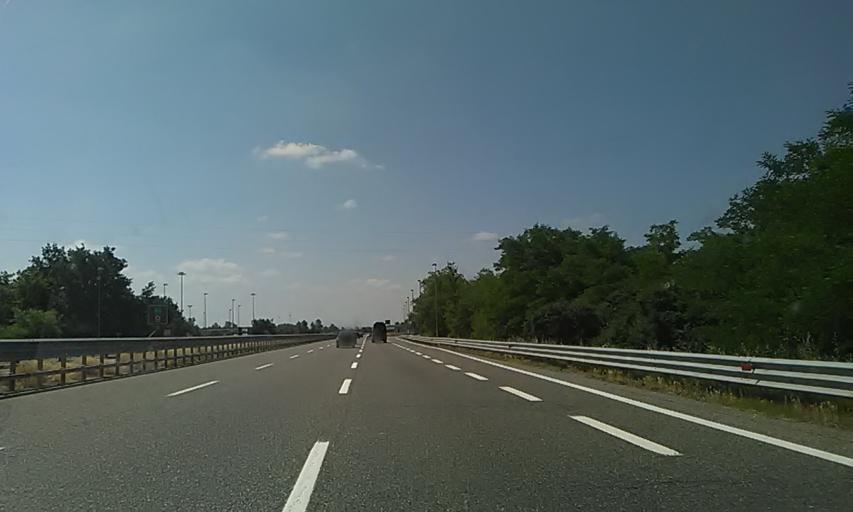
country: IT
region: Piedmont
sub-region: Provincia di Alessandria
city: Castelspina
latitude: 44.8228
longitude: 8.5939
